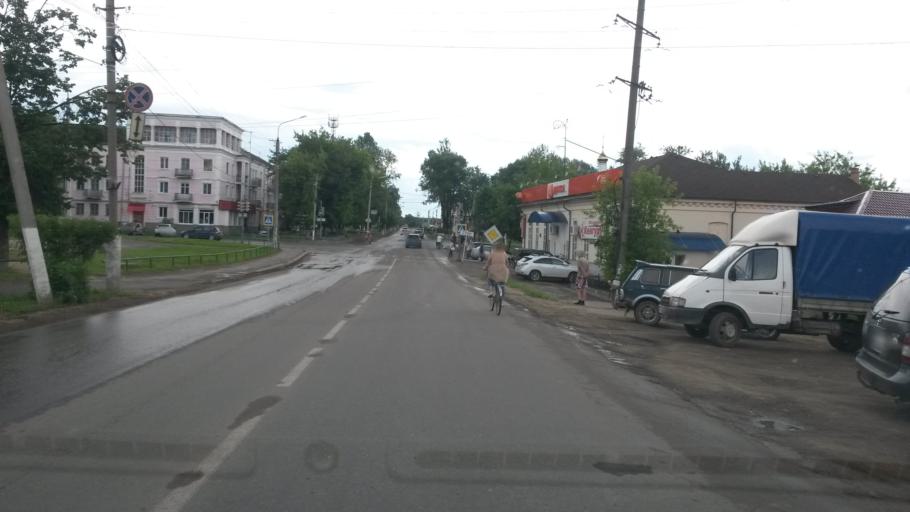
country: RU
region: Jaroslavl
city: Gavrilov-Yam
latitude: 57.3055
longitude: 39.8531
